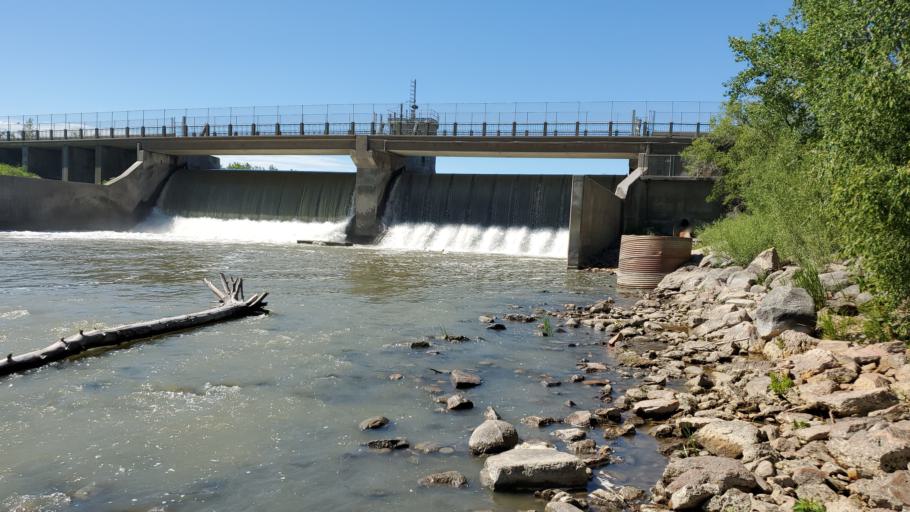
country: CA
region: Manitoba
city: Portage la Prairie
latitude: 49.9470
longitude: -98.3292
